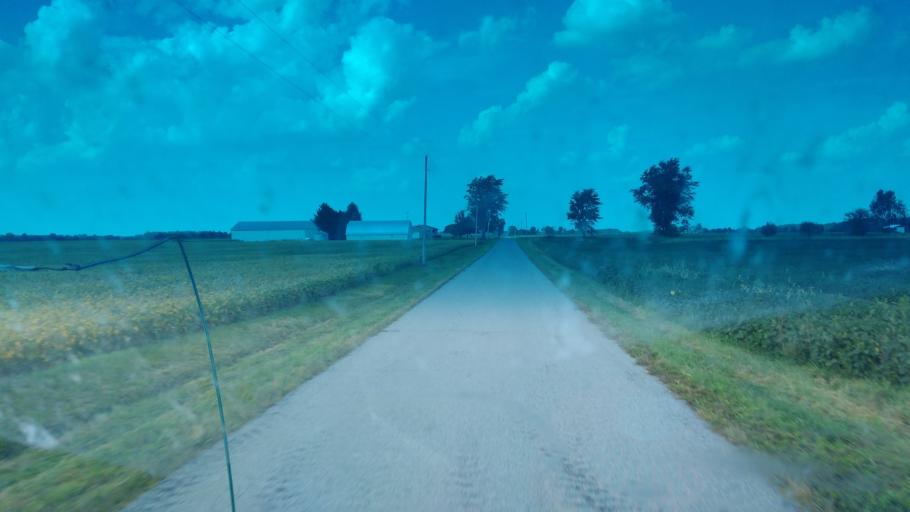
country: US
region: Ohio
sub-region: Hancock County
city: Arlington
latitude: 40.8553
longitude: -83.5856
